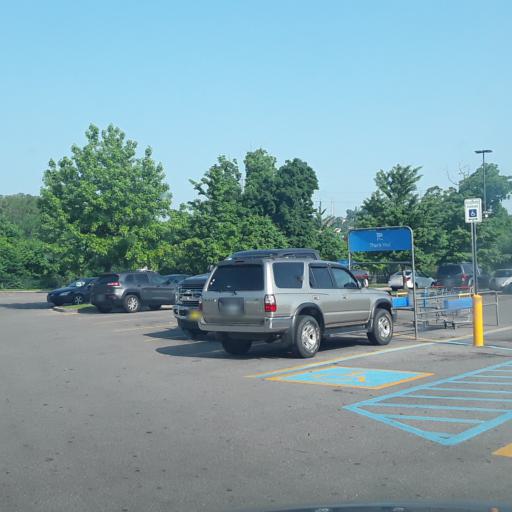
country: US
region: Tennessee
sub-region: Williamson County
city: Brentwood Estates
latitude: 36.0412
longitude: -86.7100
